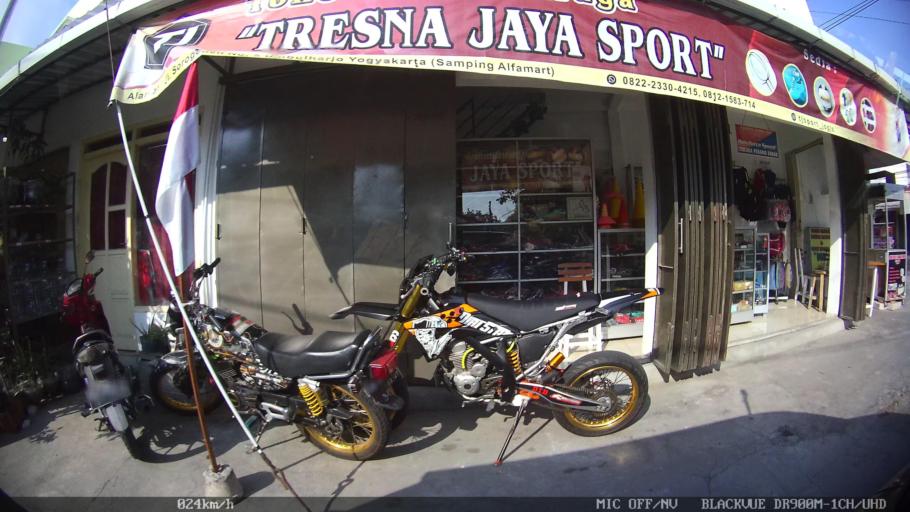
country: ID
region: Daerah Istimewa Yogyakarta
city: Yogyakarta
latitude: -7.8244
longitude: 110.3802
